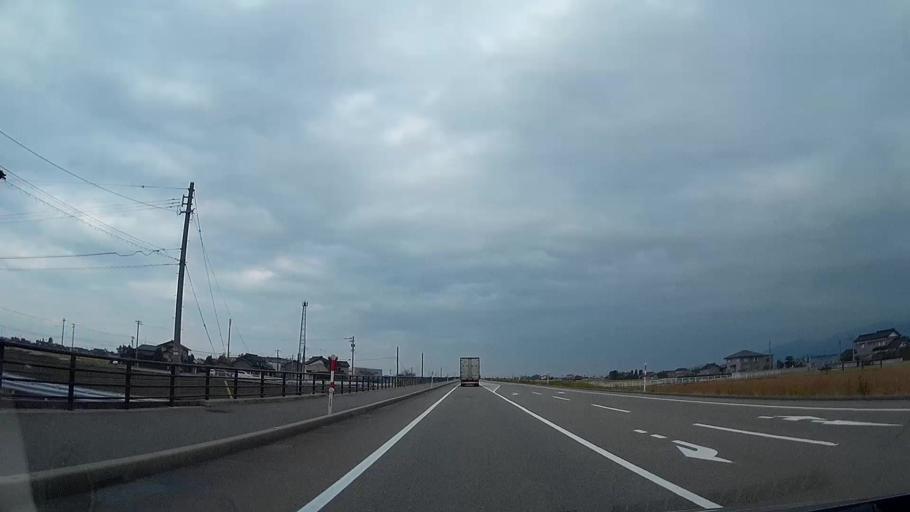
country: JP
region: Toyama
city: Nyuzen
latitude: 36.9215
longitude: 137.4676
